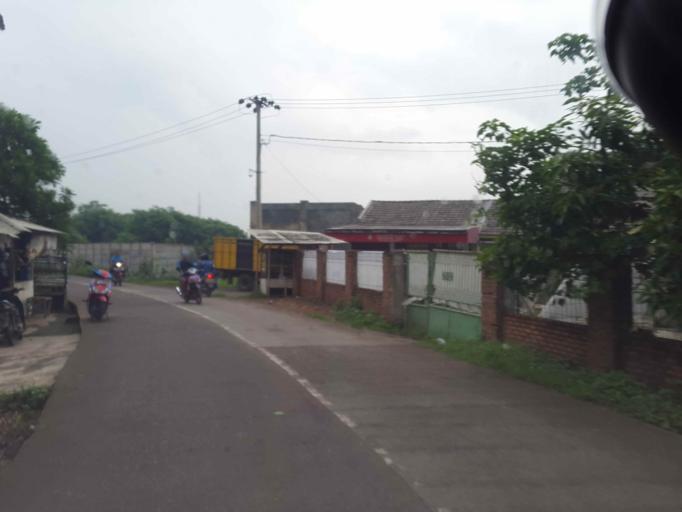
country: ID
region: West Java
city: Cikarang
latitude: -6.3031
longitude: 107.1830
